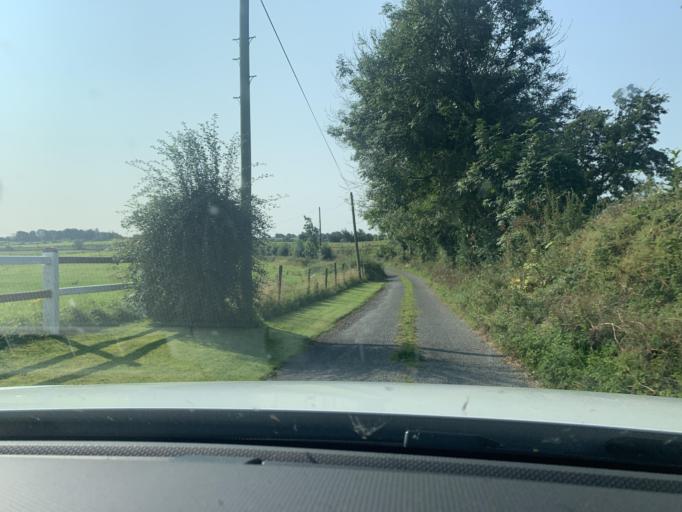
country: IE
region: Connaught
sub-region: Maigh Eo
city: Ballyhaunis
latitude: 53.7971
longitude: -8.7439
